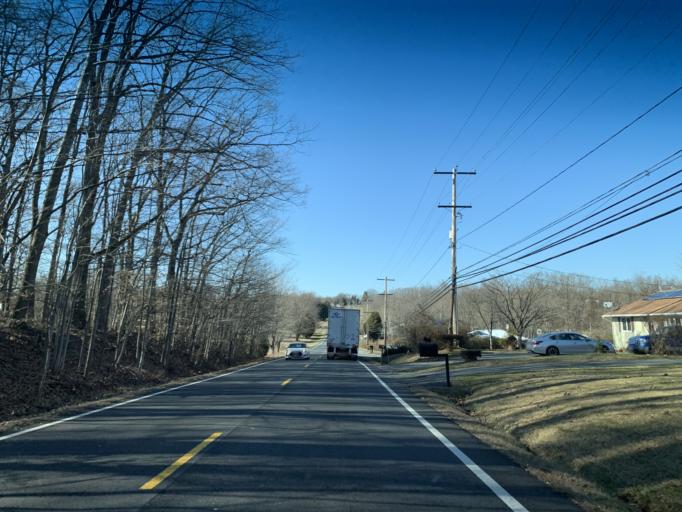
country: US
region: Maryland
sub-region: Cecil County
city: North East
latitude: 39.6637
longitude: -75.8946
